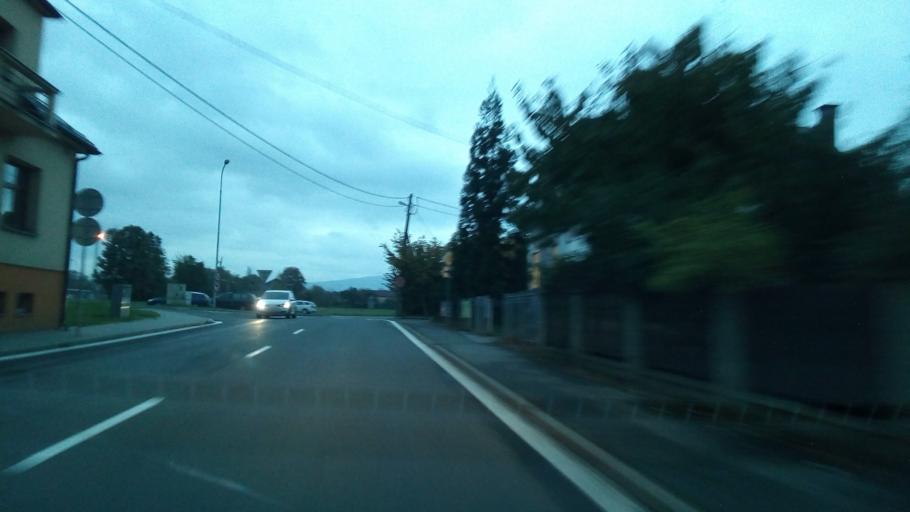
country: CZ
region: Moravskoslezsky
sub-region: Okres Frydek-Mistek
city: Frydek-Mistek
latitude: 49.6786
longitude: 18.3504
